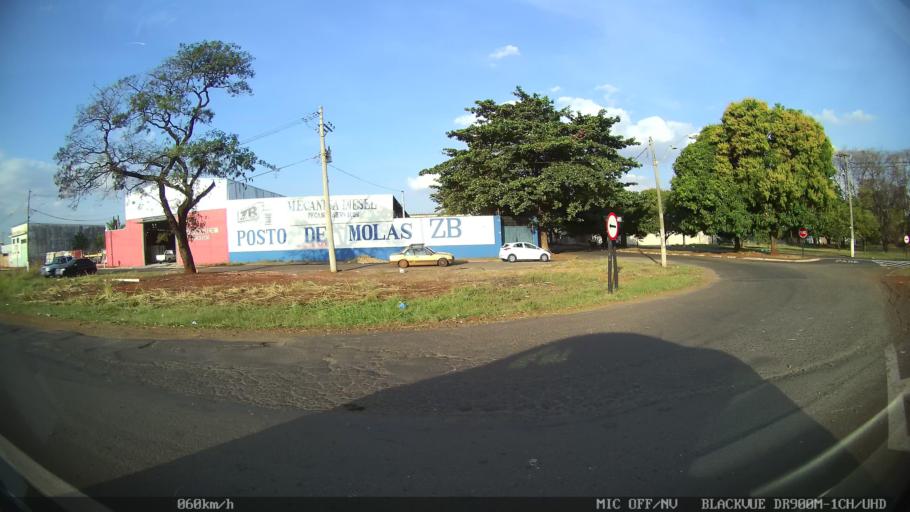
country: BR
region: Sao Paulo
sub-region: Ribeirao Preto
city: Ribeirao Preto
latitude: -21.1206
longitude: -47.7860
